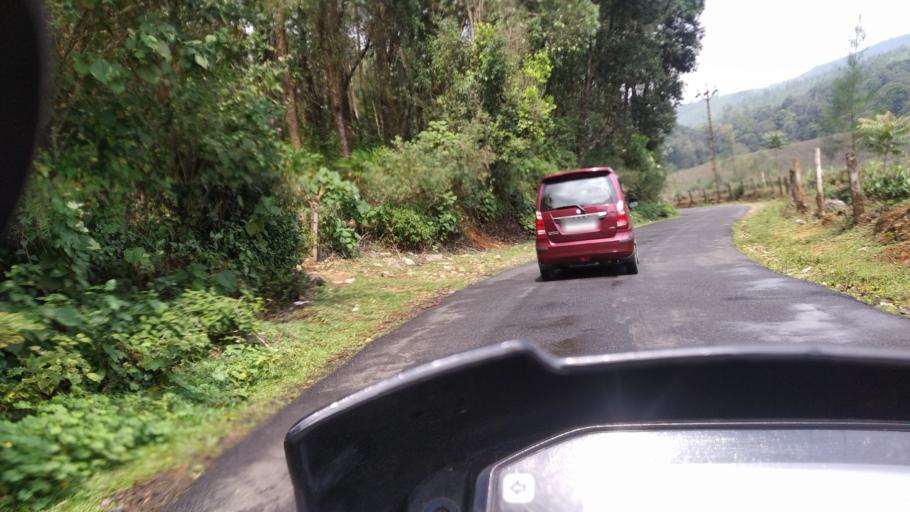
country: IN
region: Kerala
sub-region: Kottayam
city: Erattupetta
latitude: 9.6316
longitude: 76.9628
